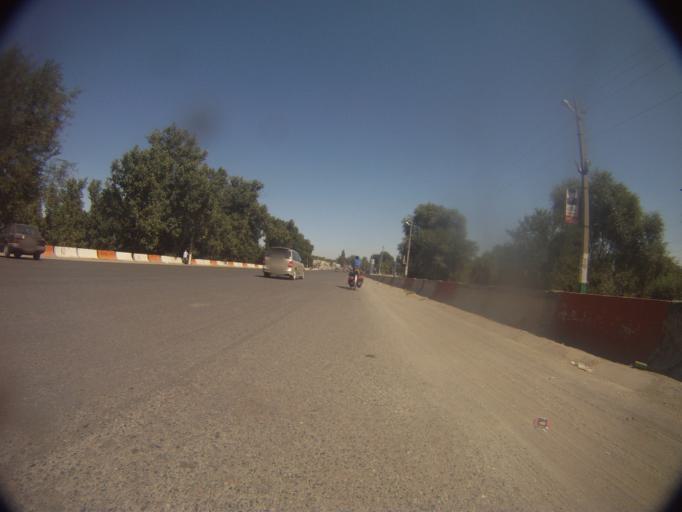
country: KG
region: Chuy
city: Sokuluk
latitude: 42.8566
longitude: 74.2869
